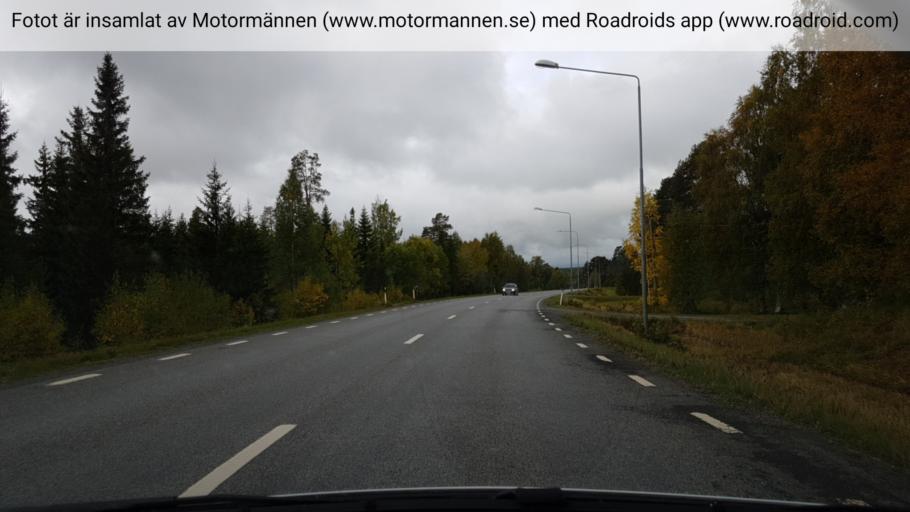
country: SE
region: Jaemtland
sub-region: OEstersunds Kommun
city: Lit
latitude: 63.3896
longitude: 14.9575
